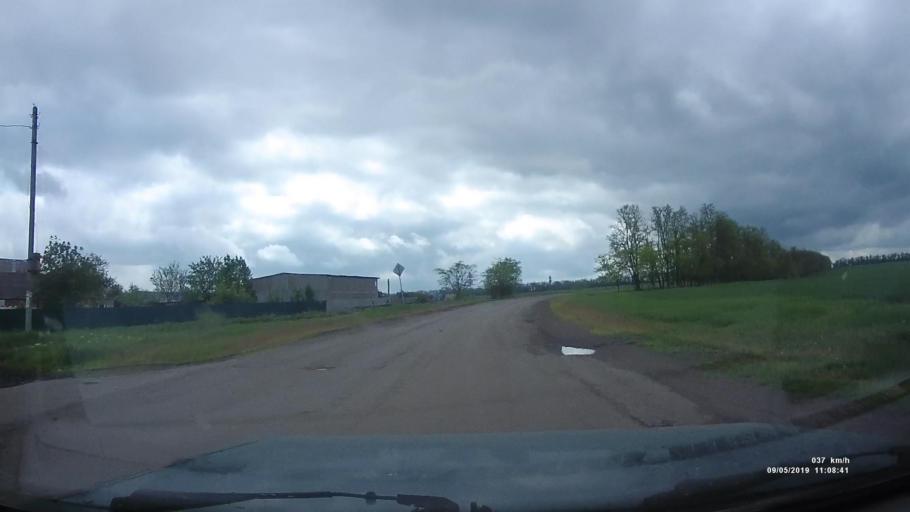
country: RU
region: Krasnodarskiy
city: Kanelovskaya
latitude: 46.7884
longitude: 39.2109
